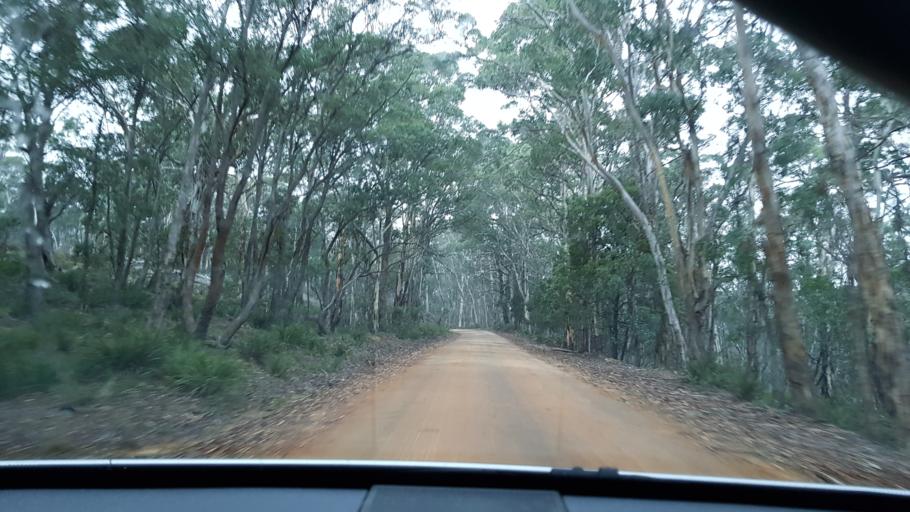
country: AU
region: New South Wales
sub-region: Oberon
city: Oberon
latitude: -33.9783
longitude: 150.0551
